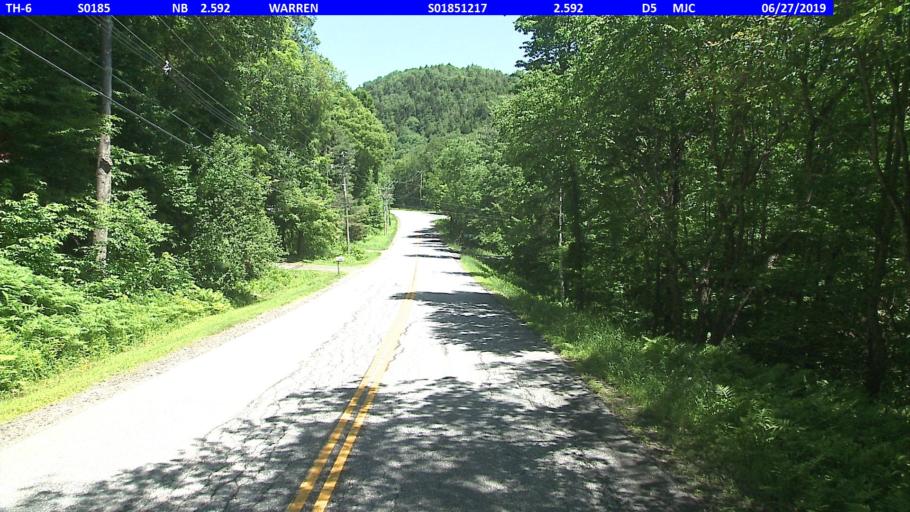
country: US
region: Vermont
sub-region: Addison County
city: Bristol
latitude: 44.1532
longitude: -72.8801
